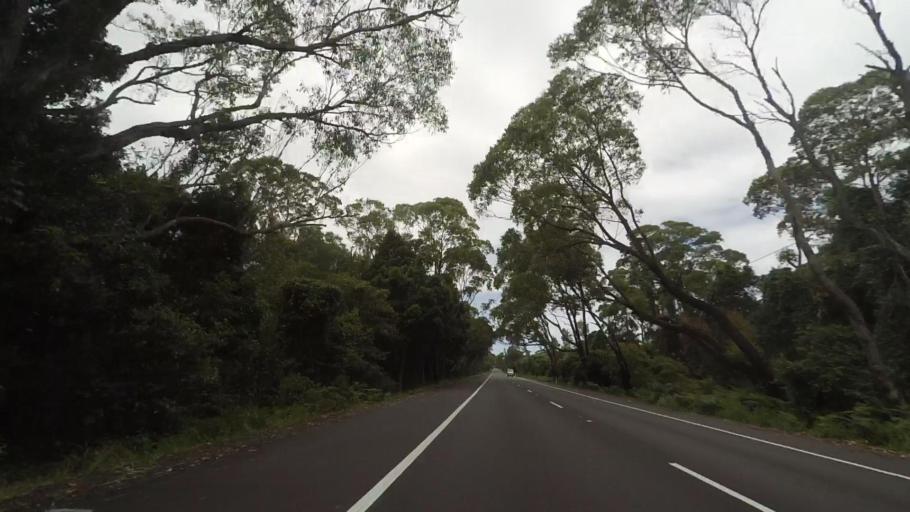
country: AU
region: New South Wales
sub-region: Wyong Shire
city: Noraville
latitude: -33.3030
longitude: 151.5281
